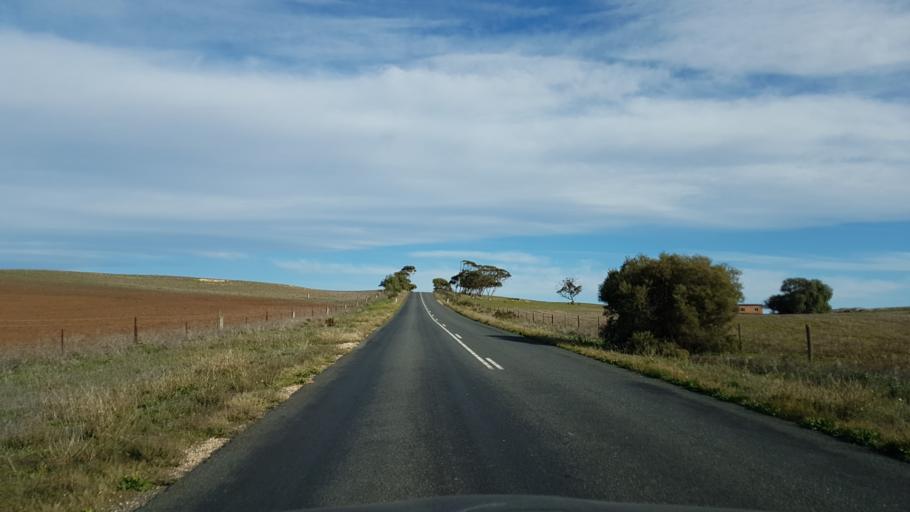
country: AU
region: South Australia
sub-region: Murray Bridge
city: Tailem Bend
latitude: -35.1832
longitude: 139.4632
